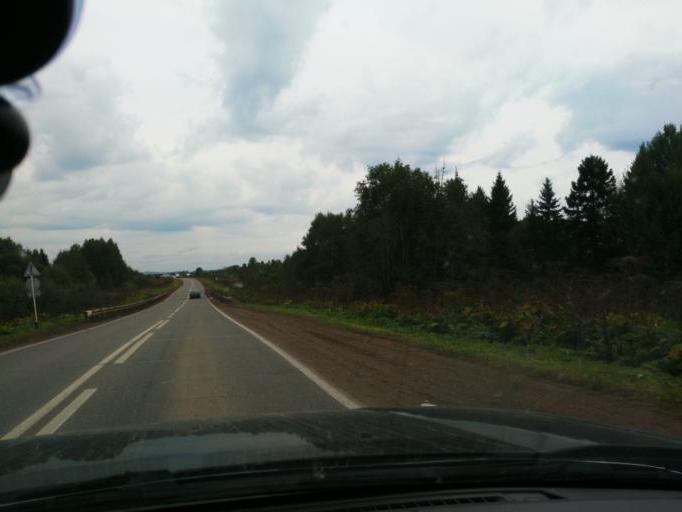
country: RU
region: Perm
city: Chernushka
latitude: 56.7221
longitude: 56.1797
